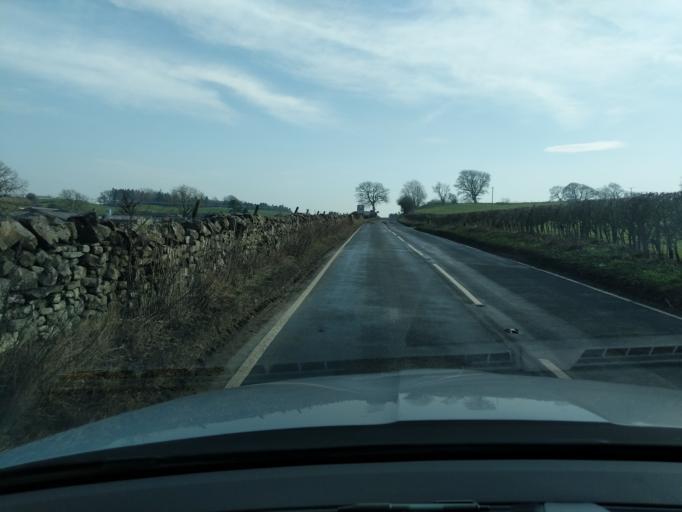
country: GB
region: England
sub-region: North Yorkshire
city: Leyburn
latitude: 54.3519
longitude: -1.8102
